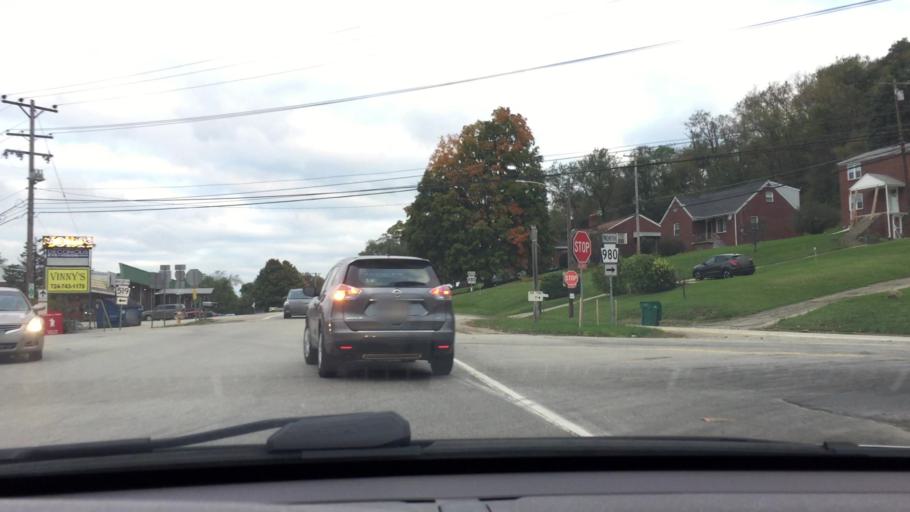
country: US
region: Pennsylvania
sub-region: Washington County
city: Canonsburg
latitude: 40.2424
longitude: -80.1809
